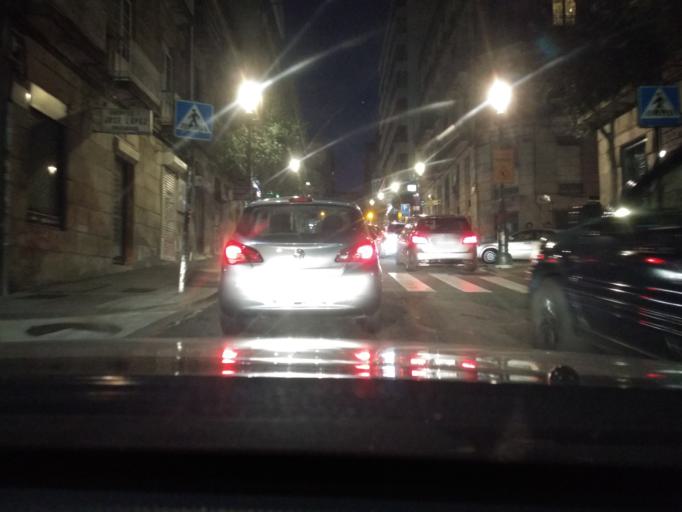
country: ES
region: Galicia
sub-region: Provincia de Pontevedra
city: Vigo
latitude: 42.2356
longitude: -8.7169
